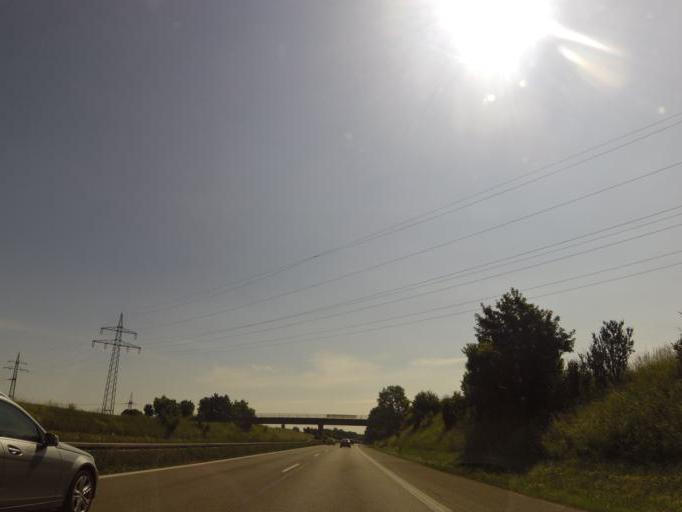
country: DE
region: Baden-Wuerttemberg
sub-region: Tuebingen Region
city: Beimerstetten
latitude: 48.4580
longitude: 9.9894
